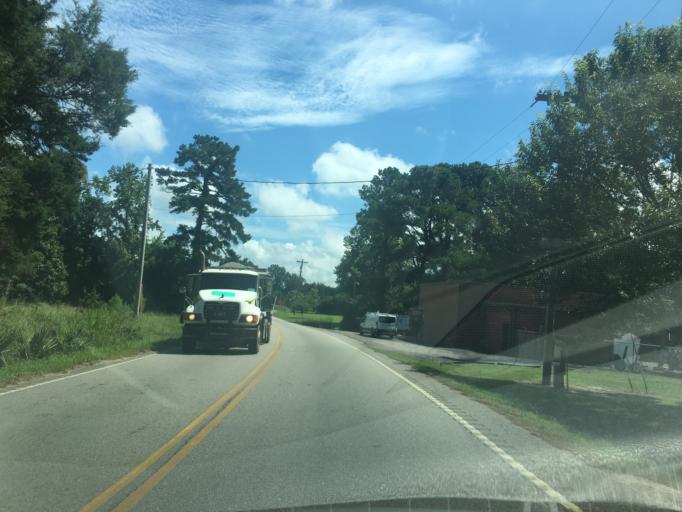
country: US
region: South Carolina
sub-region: Horry County
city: North Myrtle Beach
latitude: 33.8626
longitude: -78.7264
